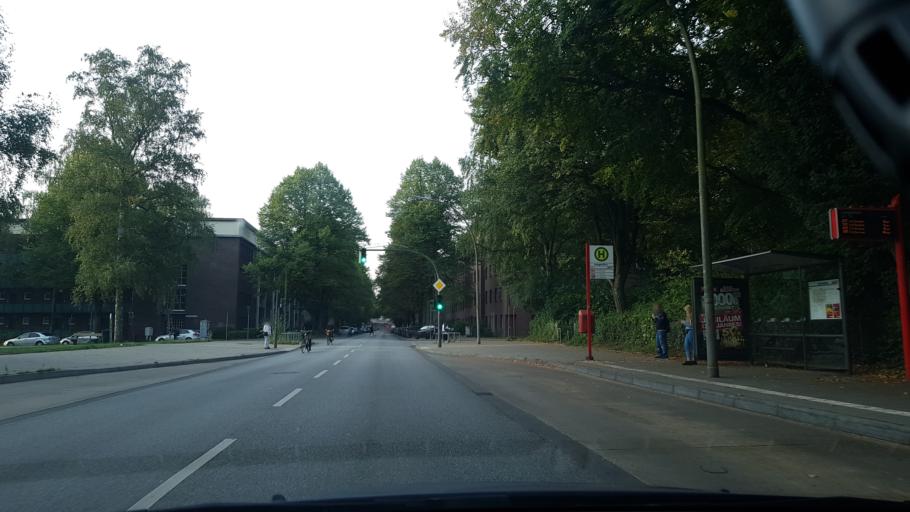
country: DE
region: Hamburg
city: Barmbek-Nord
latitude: 53.6000
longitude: 10.0507
